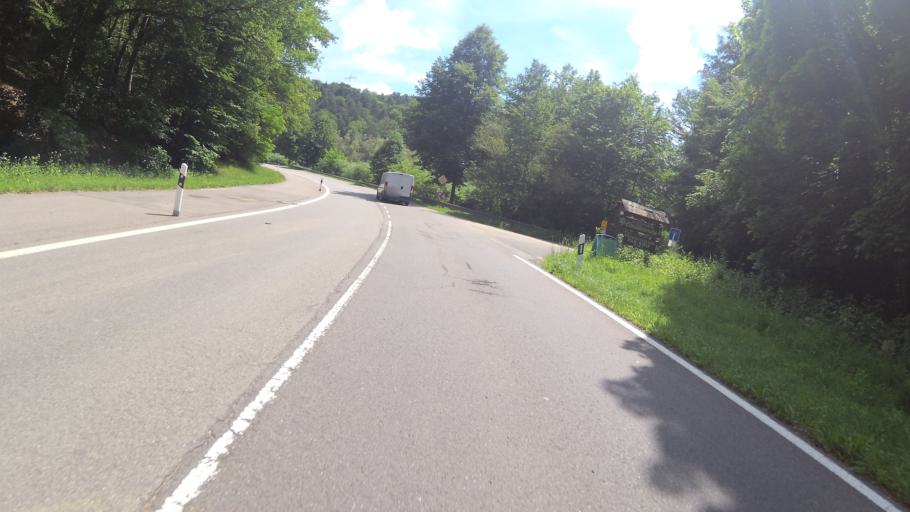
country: DE
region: Saarland
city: Homburg
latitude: 49.3003
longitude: 7.3528
